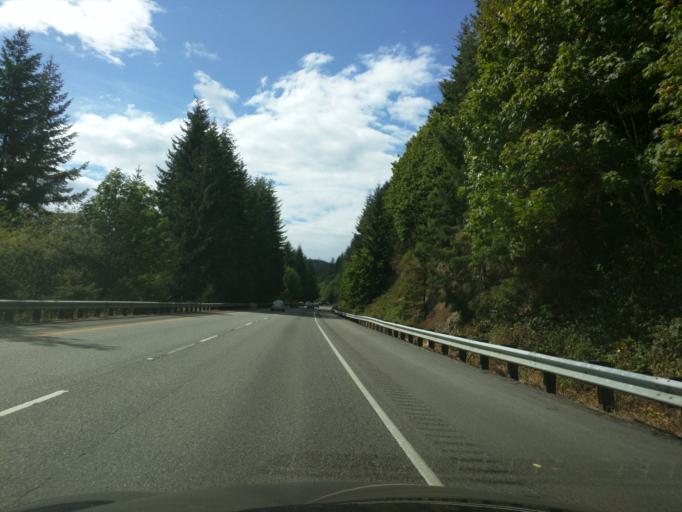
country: US
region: Washington
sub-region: Whatcom County
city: Sudden Valley
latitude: 48.6698
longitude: -122.3786
